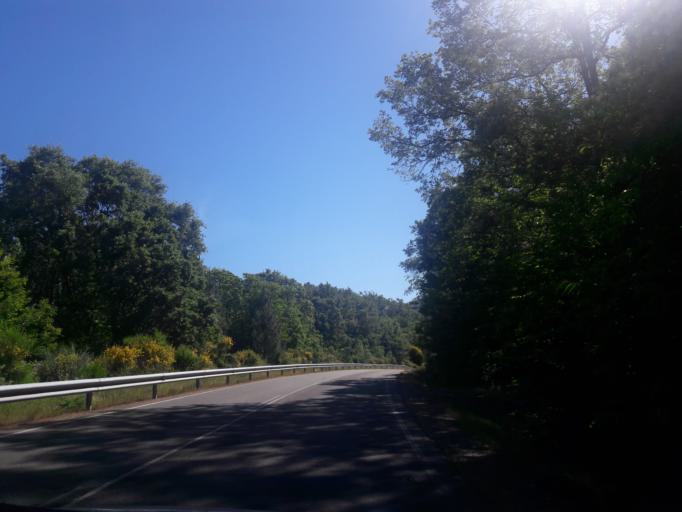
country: ES
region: Castille and Leon
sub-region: Provincia de Salamanca
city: Puerto de Bejar
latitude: 40.3496
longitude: -5.8500
